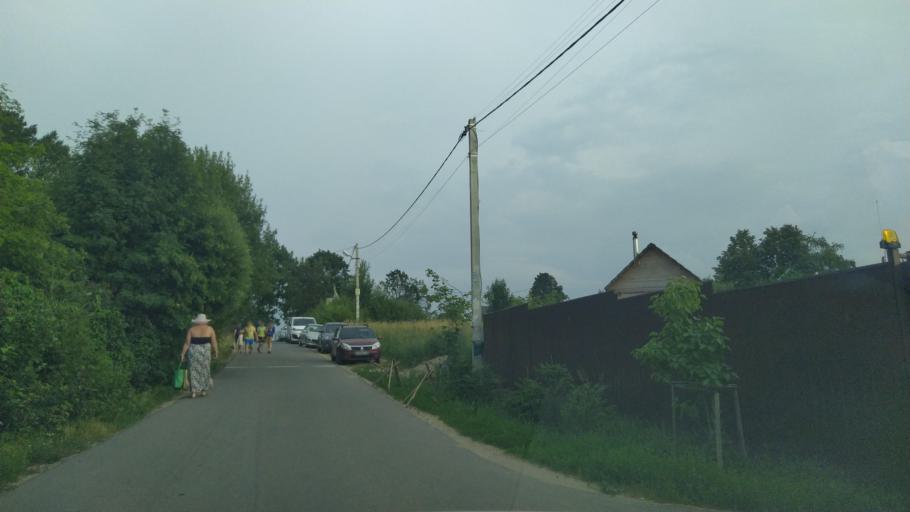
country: RU
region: Leningrad
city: Koltushi
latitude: 59.8914
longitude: 30.7321
